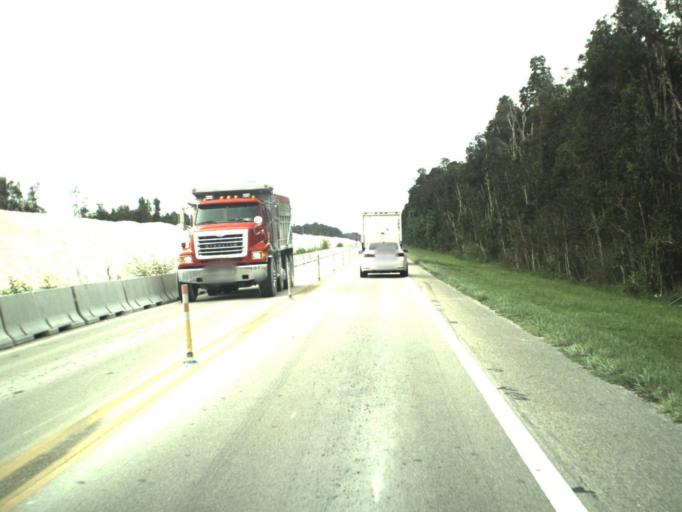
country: US
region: Florida
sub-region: Miami-Dade County
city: Kendall West
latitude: 25.7501
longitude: -80.4810
